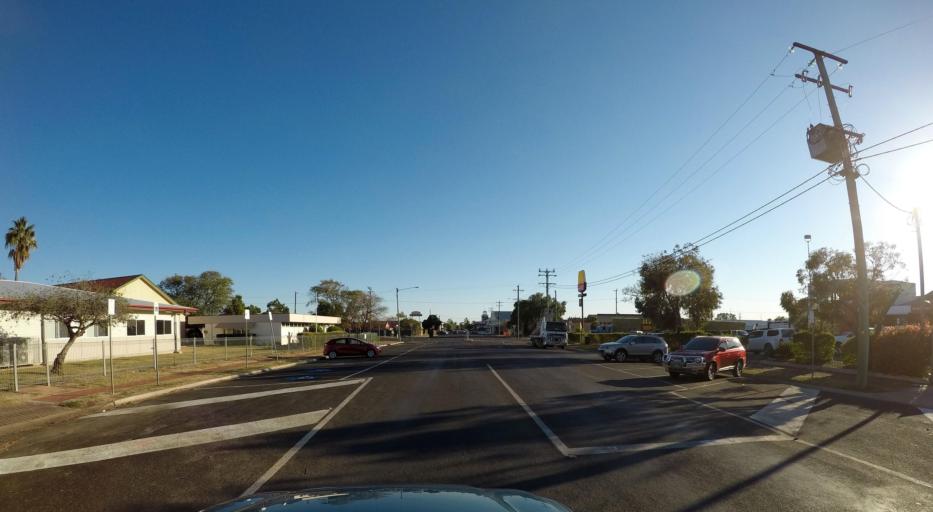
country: AU
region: Queensland
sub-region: Maranoa
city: Roma
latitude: -26.5744
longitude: 148.7880
